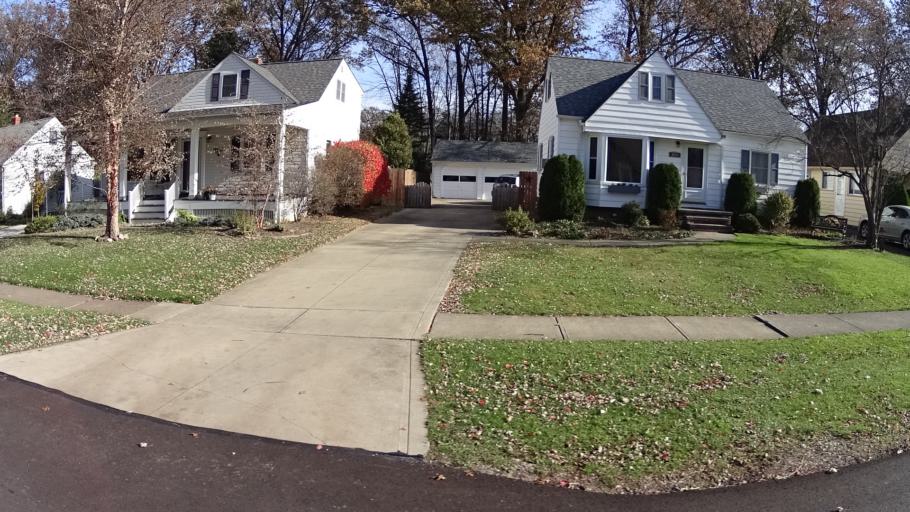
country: US
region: Ohio
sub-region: Lorain County
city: Avon Lake
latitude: 41.5084
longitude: -81.9950
